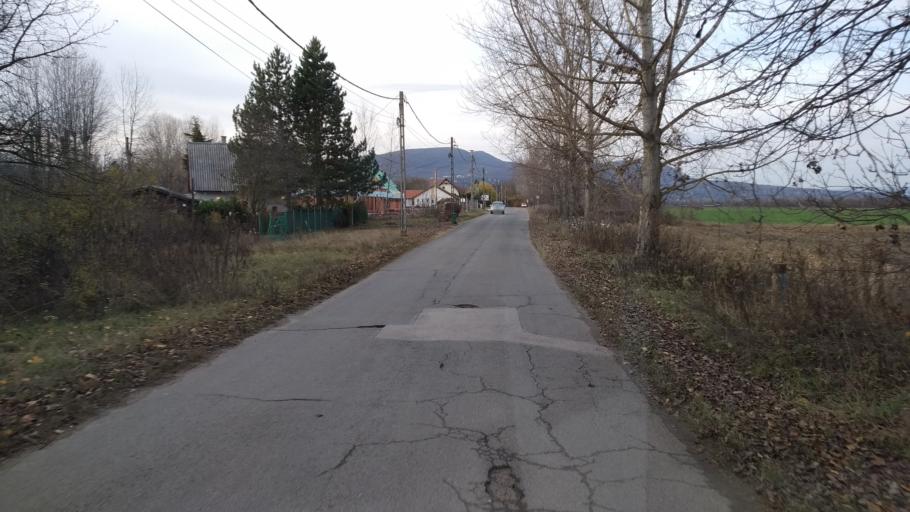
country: HU
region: Pest
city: God
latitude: 47.6855
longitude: 19.1145
